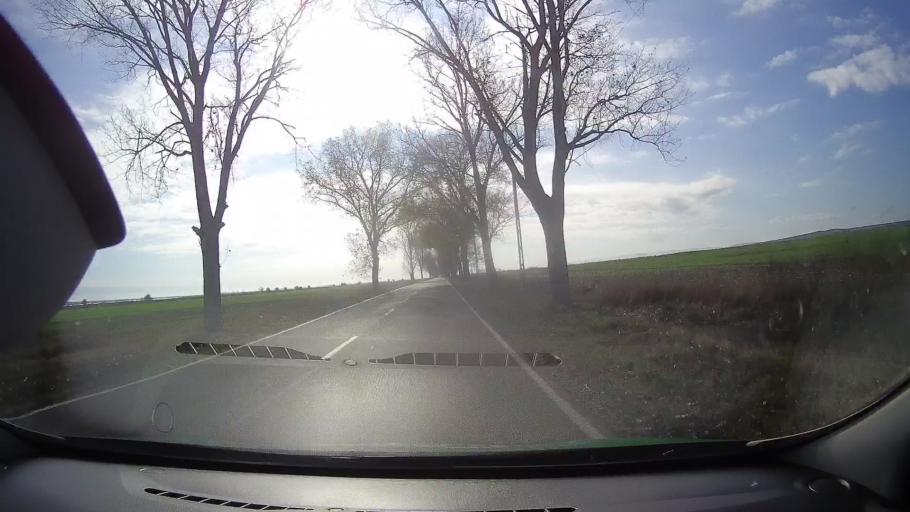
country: RO
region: Tulcea
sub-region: Comuna Valea Nucarilor
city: Agighiol
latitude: 45.0125
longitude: 28.8840
